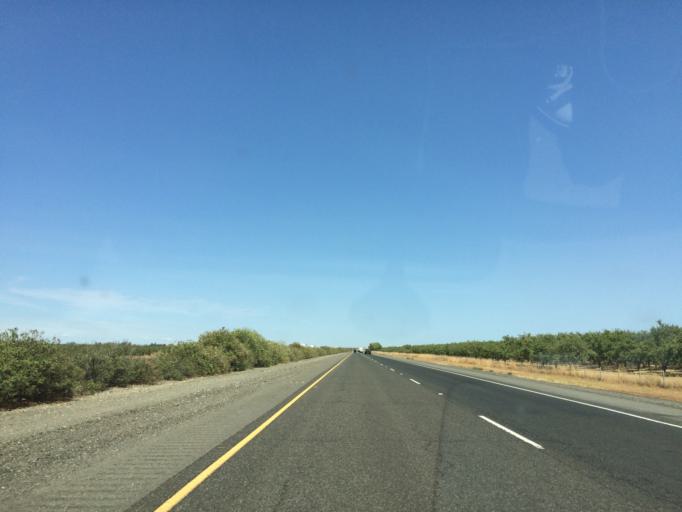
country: US
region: California
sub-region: Glenn County
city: Orland
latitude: 39.6531
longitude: -122.2044
